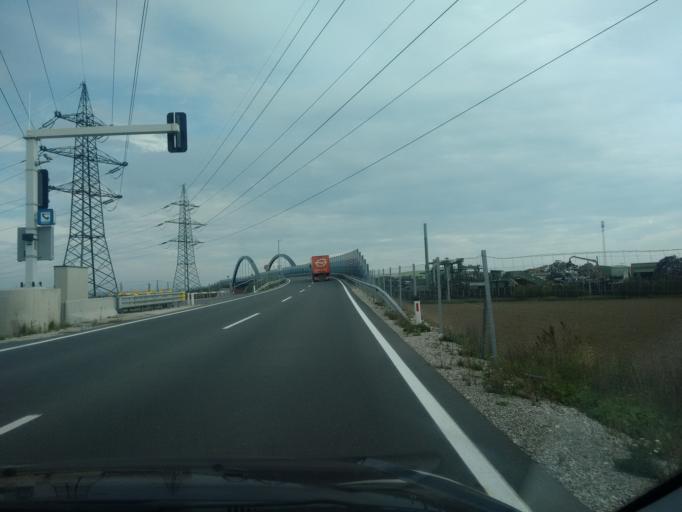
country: AT
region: Upper Austria
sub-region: Wels-Land
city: Edt bei Lambach
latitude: 48.1027
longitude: 13.8978
